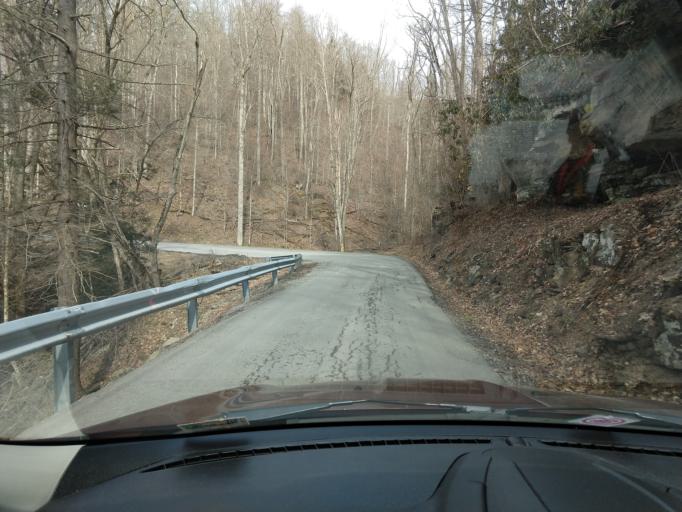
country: US
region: West Virginia
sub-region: Tucker County
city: Parsons
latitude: 39.0330
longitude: -79.5444
